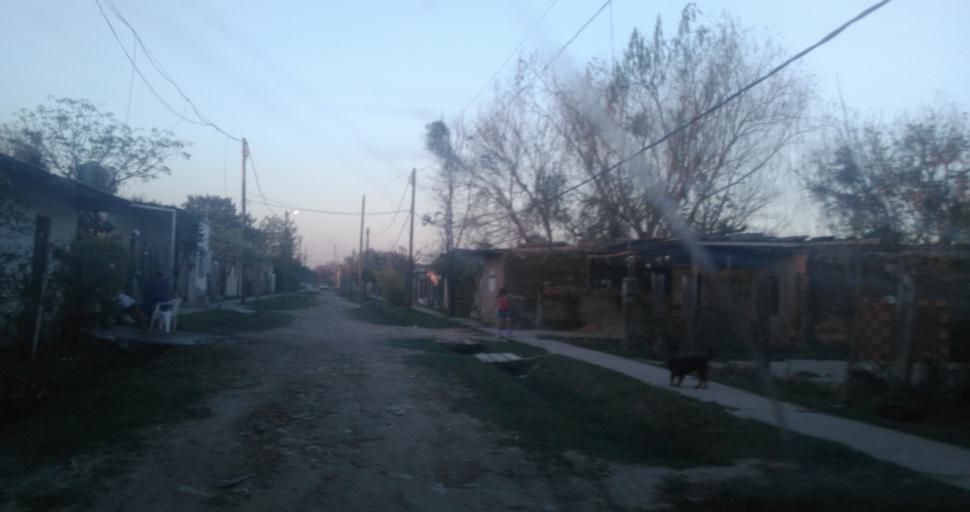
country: AR
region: Chaco
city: Resistencia
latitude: -27.4615
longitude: -59.0230
